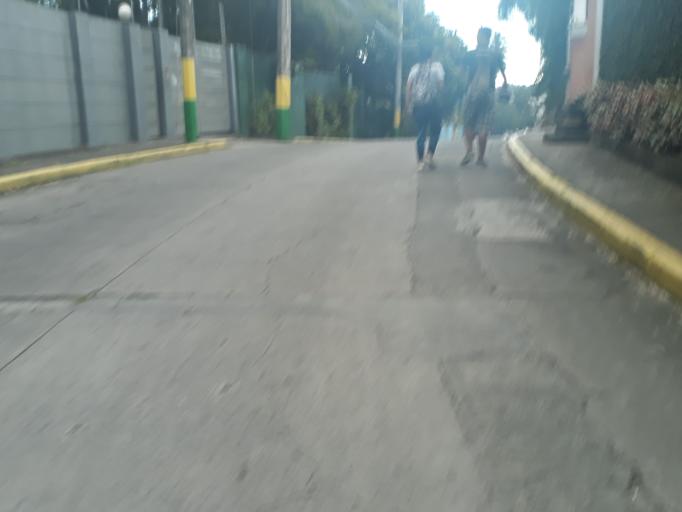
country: PH
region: Metro Manila
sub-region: Mandaluyong
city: Mandaluyong City
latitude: 14.5914
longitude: 121.0398
